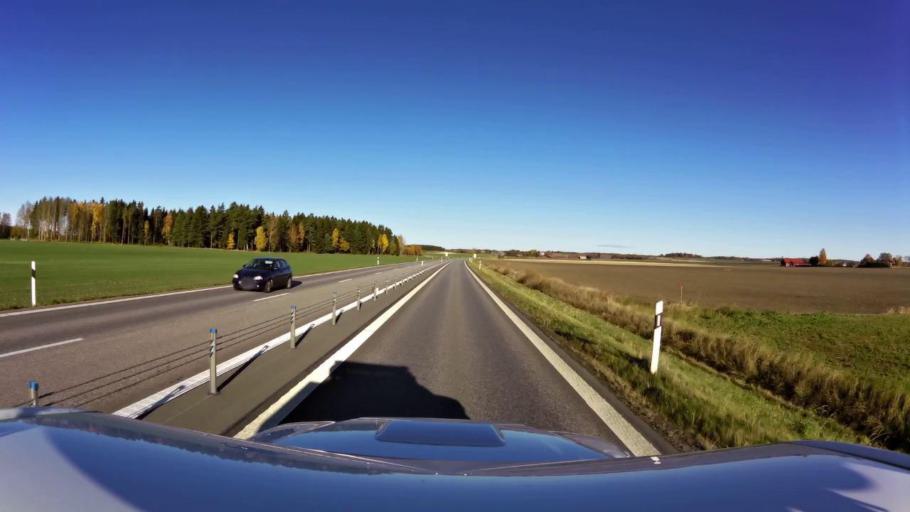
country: SE
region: OEstergoetland
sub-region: Linkopings Kommun
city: Berg
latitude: 58.4565
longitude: 15.5008
